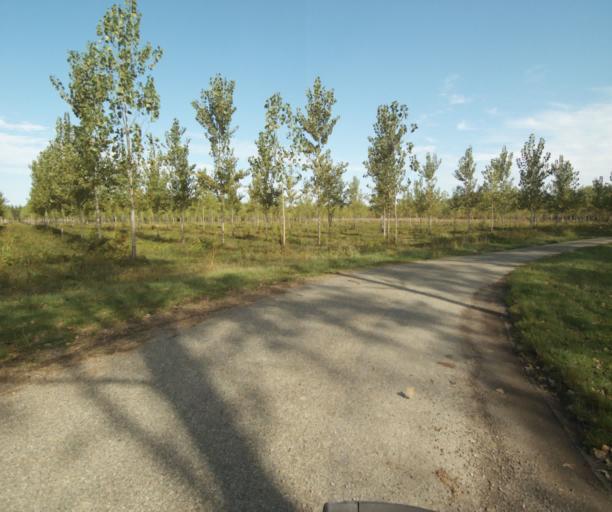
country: FR
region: Midi-Pyrenees
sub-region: Departement du Tarn-et-Garonne
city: Finhan
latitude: 43.9027
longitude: 1.2154
